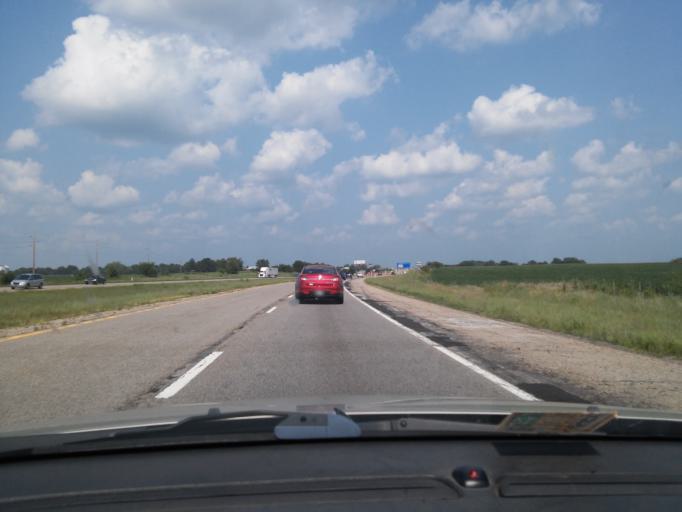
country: US
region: Illinois
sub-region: Logan County
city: Atlanta
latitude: 40.2494
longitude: -89.2427
